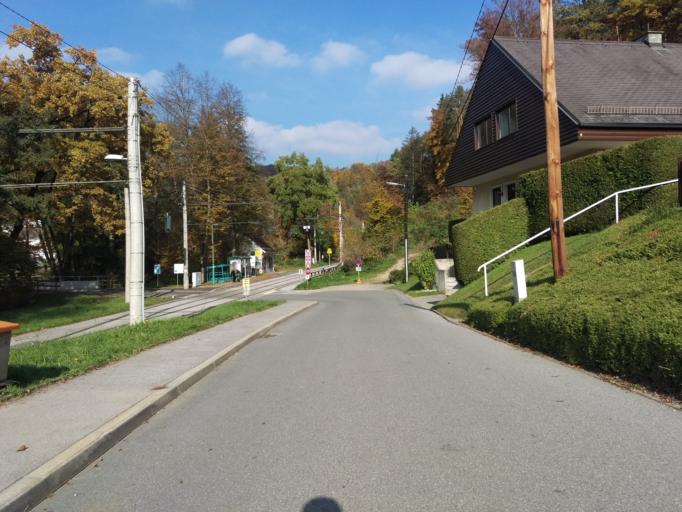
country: AT
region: Styria
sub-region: Graz Stadt
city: Mariatrost
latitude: 47.0960
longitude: 15.4694
